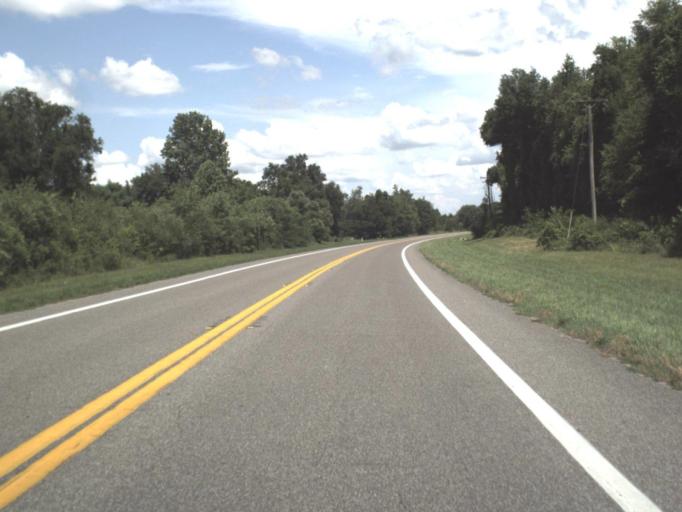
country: US
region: Florida
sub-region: Lafayette County
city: Mayo
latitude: 30.0532
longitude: -83.0933
